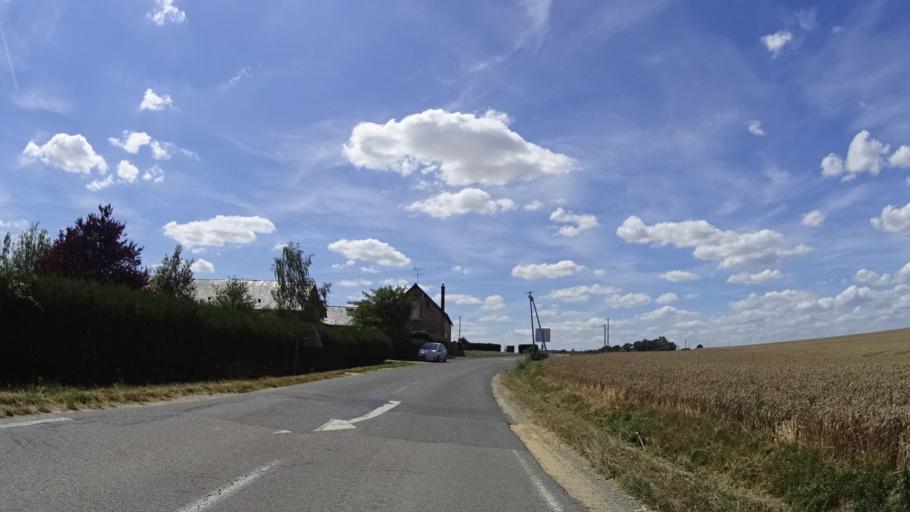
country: FR
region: Pays de la Loire
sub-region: Departement de Maine-et-Loire
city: Cande
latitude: 47.6132
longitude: -0.9876
